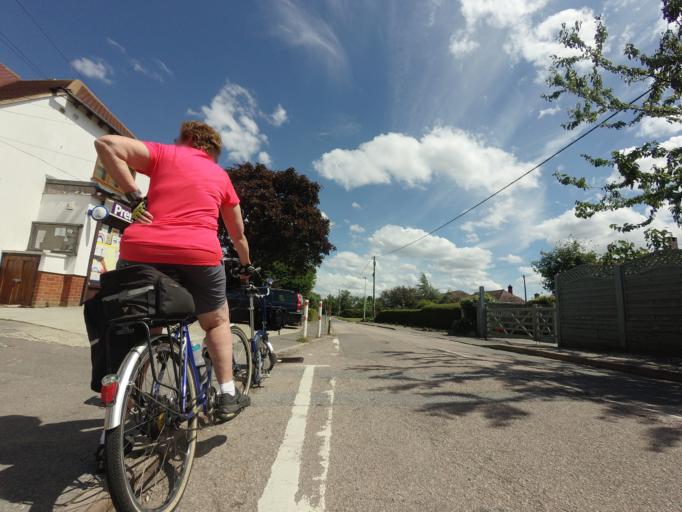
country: GB
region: England
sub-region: Medway
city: High Halstow
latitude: 51.4469
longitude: 0.5653
